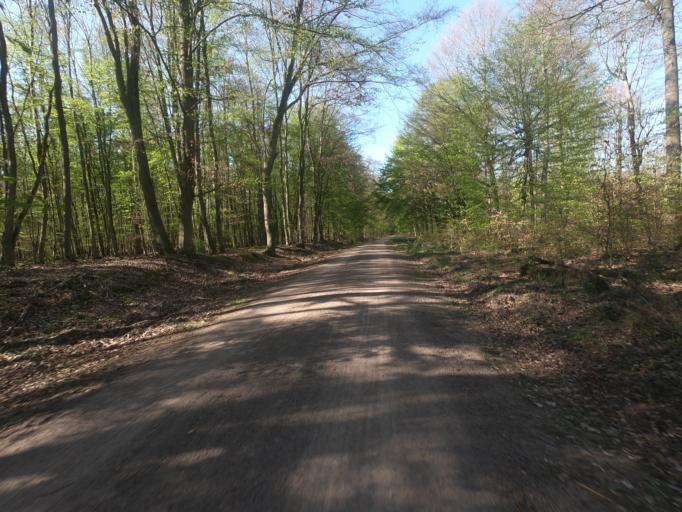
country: DE
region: Hesse
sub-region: Regierungsbezirk Darmstadt
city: Messel
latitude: 49.9587
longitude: 8.7142
